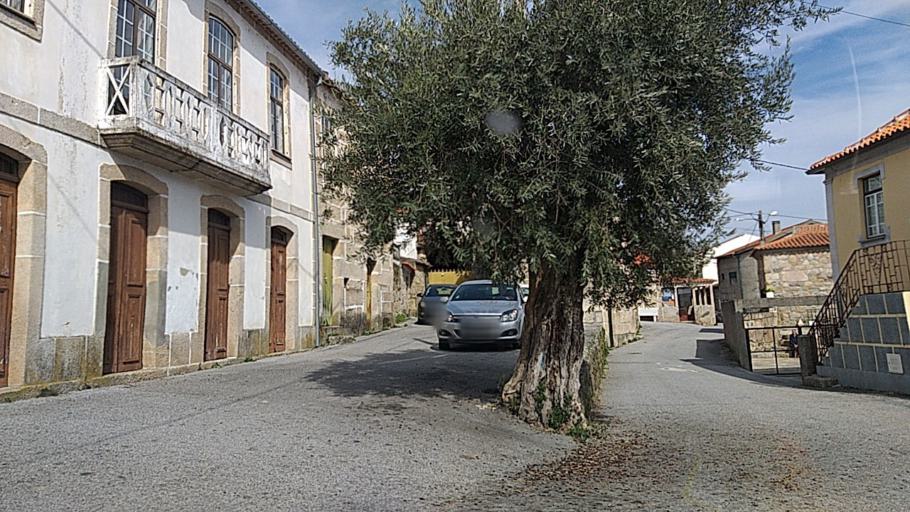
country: PT
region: Guarda
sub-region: Celorico da Beira
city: Celorico da Beira
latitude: 40.6259
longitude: -7.4383
